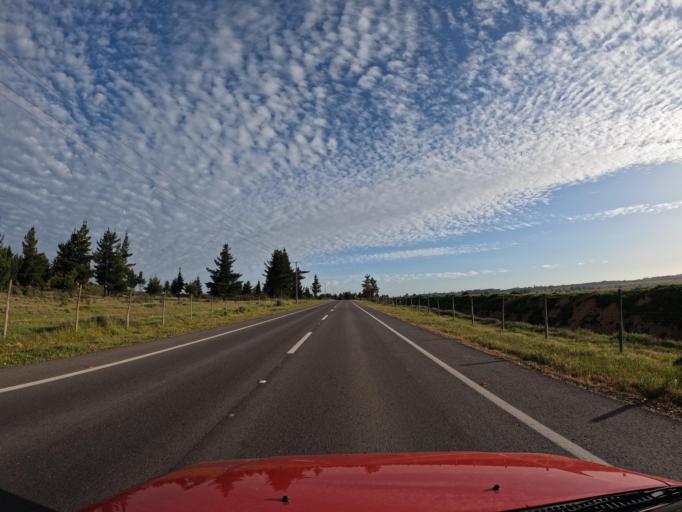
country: CL
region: Valparaiso
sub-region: San Antonio Province
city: San Antonio
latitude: -34.0629
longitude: -71.6263
